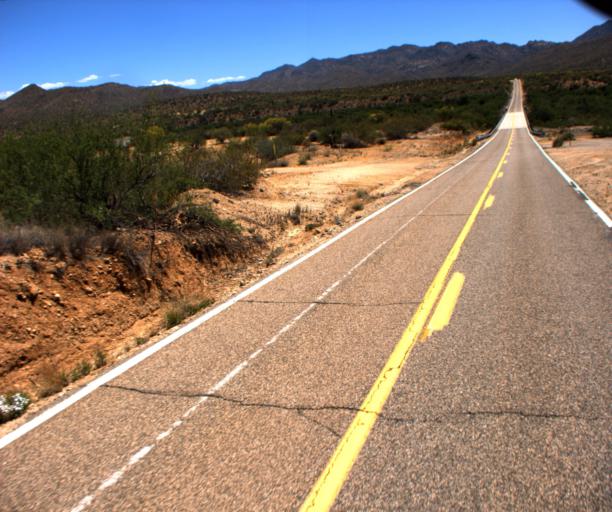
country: US
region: Arizona
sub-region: Yavapai County
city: Bagdad
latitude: 34.4822
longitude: -113.0621
